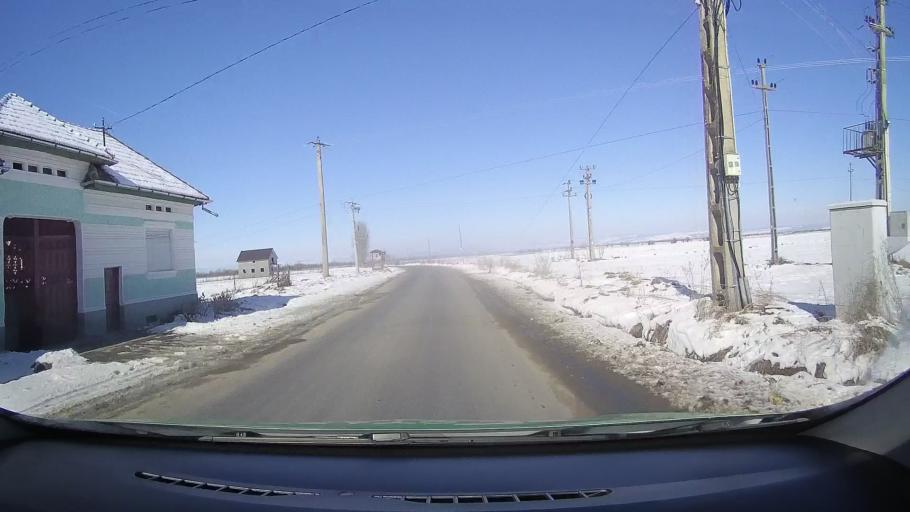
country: RO
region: Brasov
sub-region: Comuna Harseni
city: Harseni
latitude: 45.7319
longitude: 25.0279
